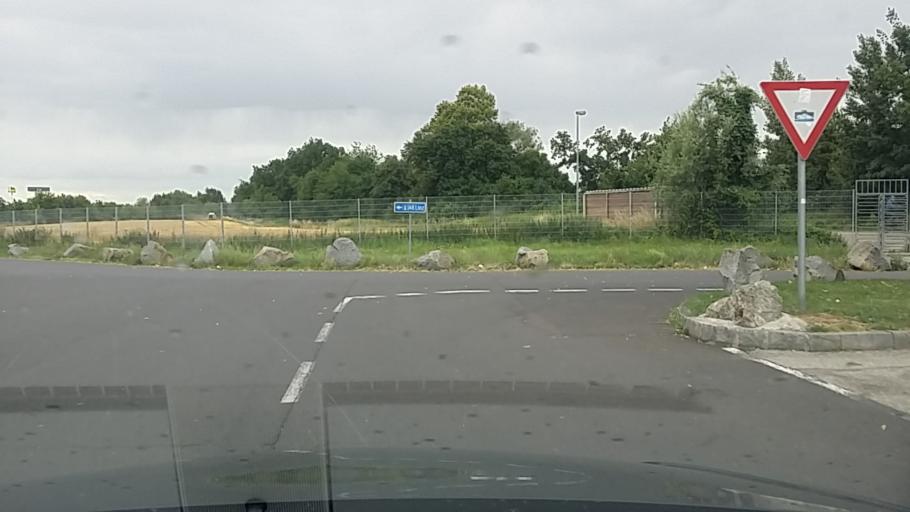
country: AT
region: Upper Austria
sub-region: Politischer Bezirk Scharding
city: Sankt Marienkirchen bei Schaerding
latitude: 48.4001
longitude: 13.4251
